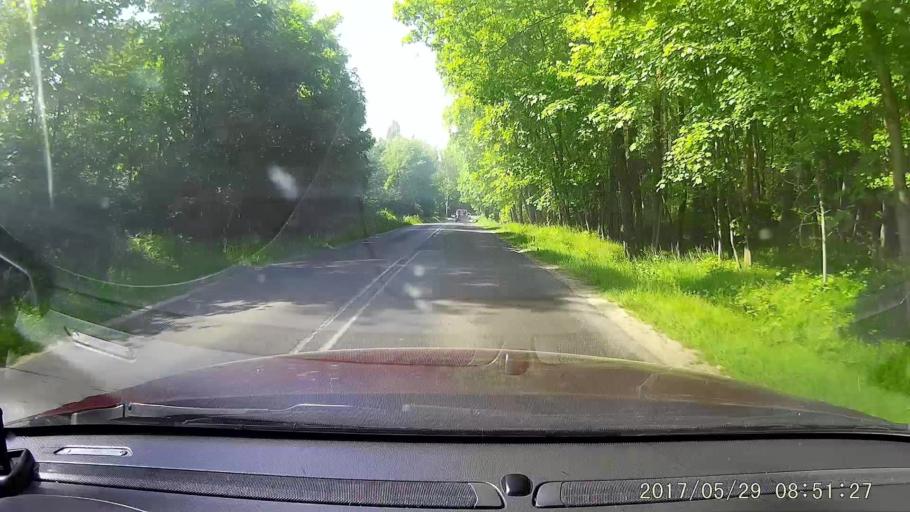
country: PL
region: Lower Silesian Voivodeship
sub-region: Powiat jeleniogorski
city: Jezow Sudecki
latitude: 50.9293
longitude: 15.7729
